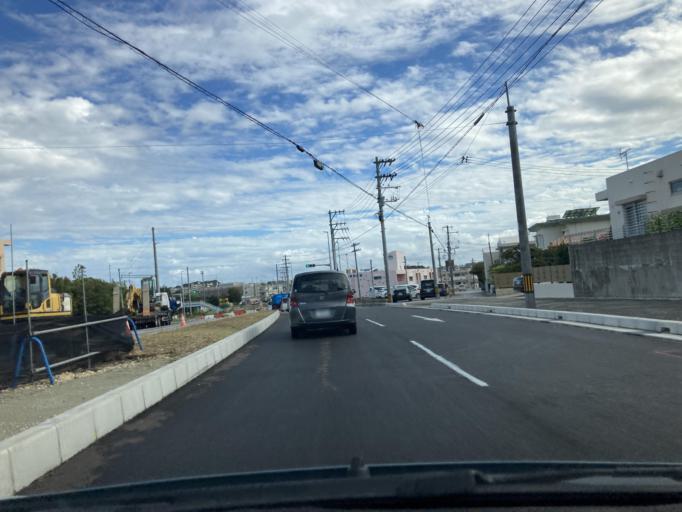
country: JP
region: Okinawa
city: Tomigusuku
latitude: 26.1523
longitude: 127.7215
